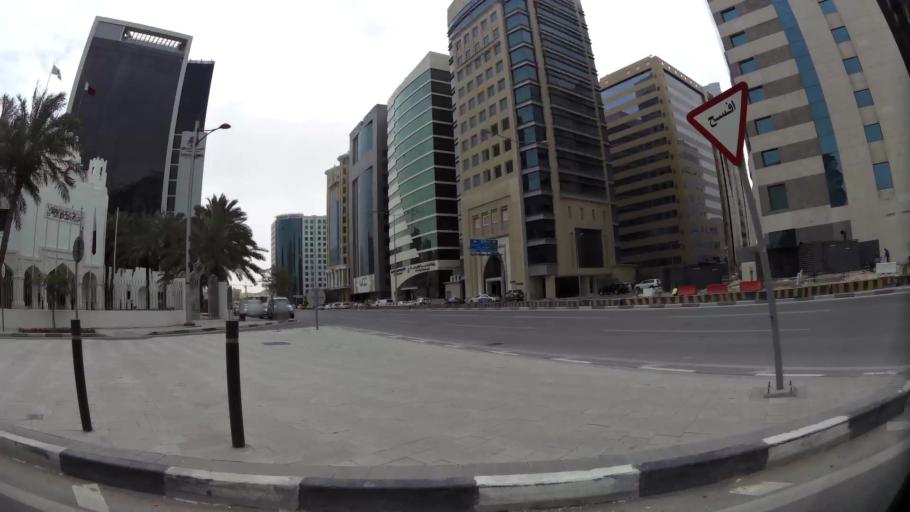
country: QA
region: Baladiyat ad Dawhah
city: Doha
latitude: 25.2898
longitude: 51.5443
